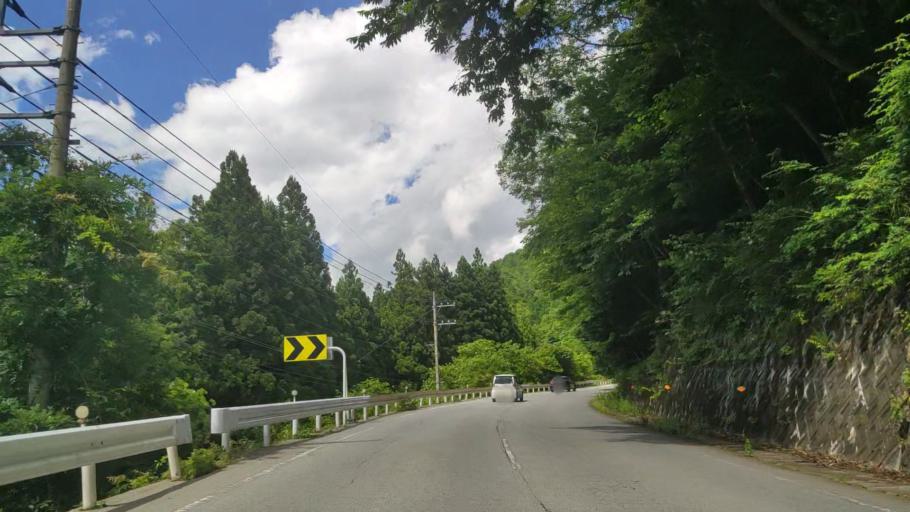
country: JP
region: Yamanashi
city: Enzan
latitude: 35.8269
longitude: 138.7637
